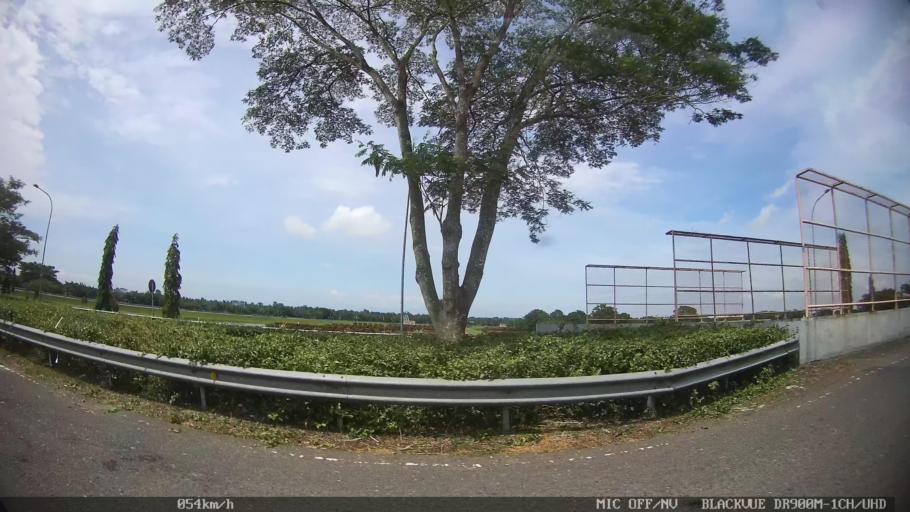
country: ID
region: North Sumatra
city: Percut
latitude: 3.6330
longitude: 98.8760
